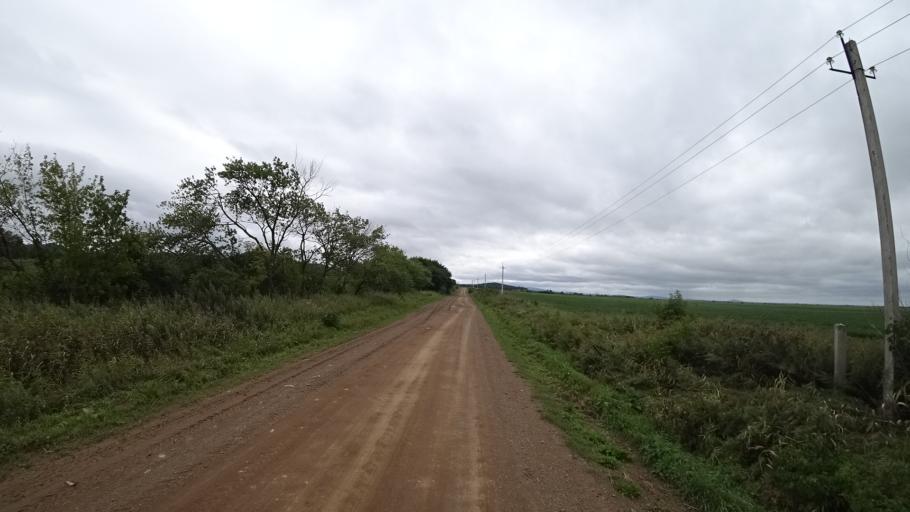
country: RU
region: Primorskiy
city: Chernigovka
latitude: 44.4878
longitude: 132.5729
